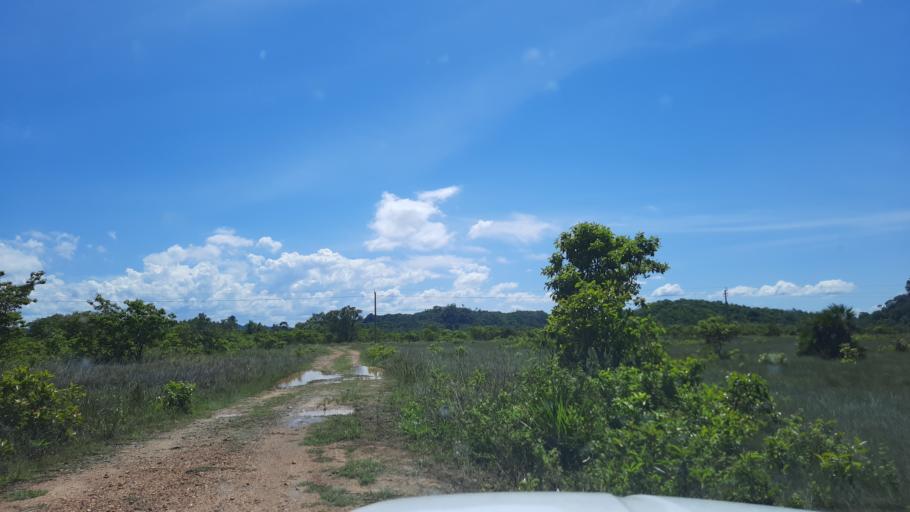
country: BZ
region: Stann Creek
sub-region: Dangriga
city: Dangriga
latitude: 17.1940
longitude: -88.3979
